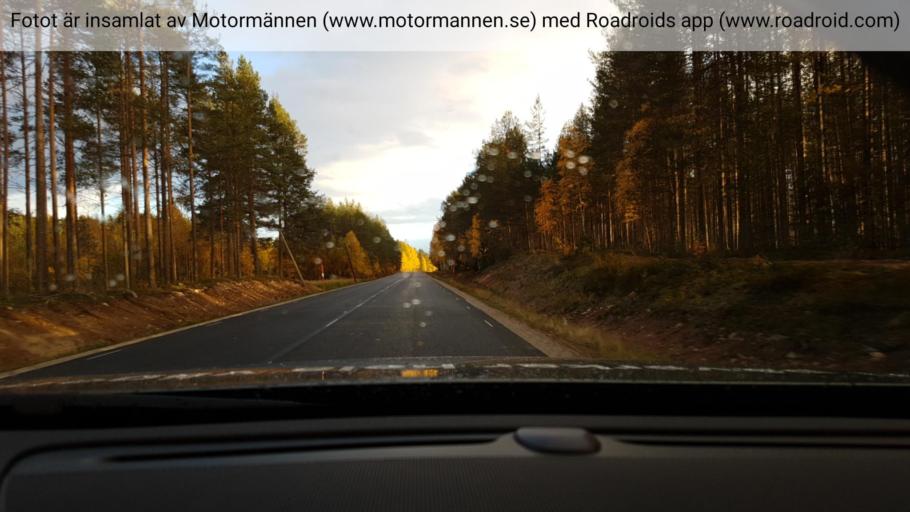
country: SE
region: Norrbotten
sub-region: Overkalix Kommun
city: OEverkalix
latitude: 66.4384
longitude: 22.7902
